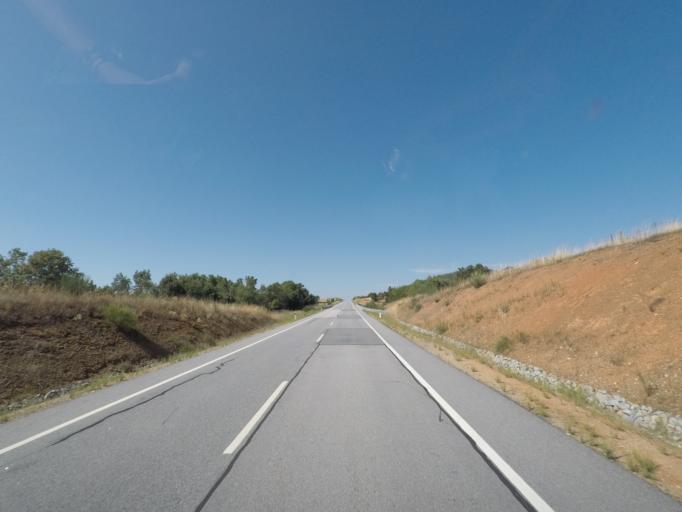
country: PT
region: Braganca
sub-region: Mogadouro
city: Mogadouro
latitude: 41.3520
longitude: -6.5961
